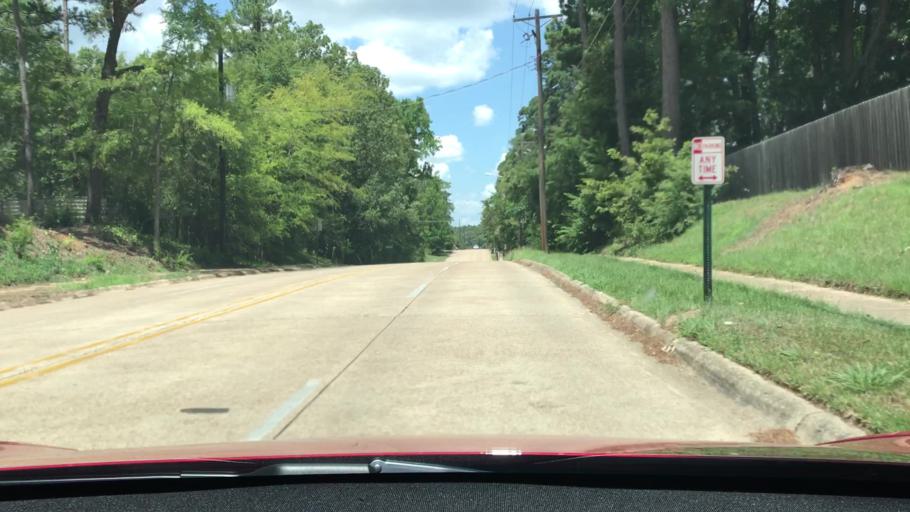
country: US
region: Louisiana
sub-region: Bossier Parish
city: Bossier City
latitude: 32.4382
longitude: -93.7344
